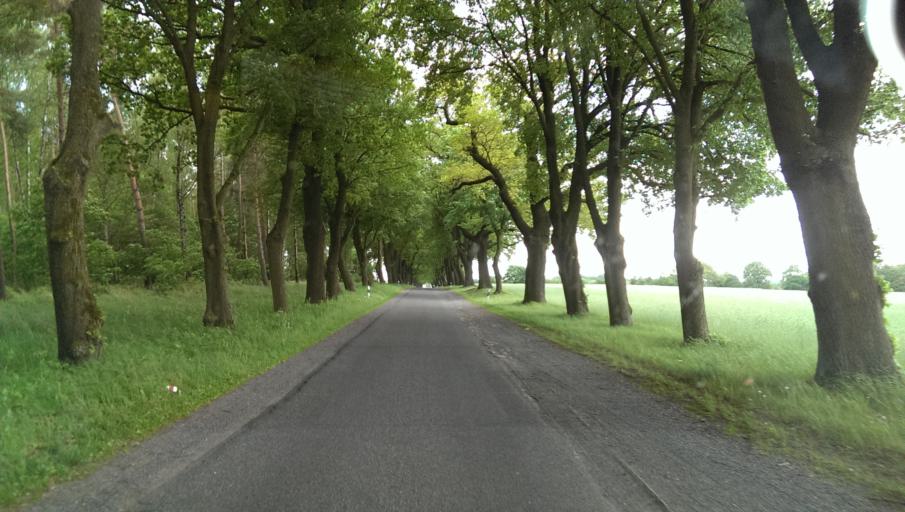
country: DE
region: Brandenburg
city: Wiesenburg
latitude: 52.1481
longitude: 12.4816
